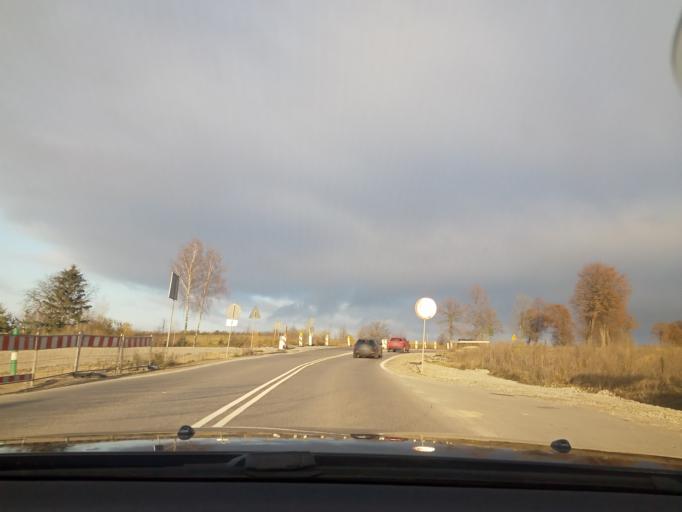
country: PL
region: Lesser Poland Voivodeship
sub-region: Powiat miechowski
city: Miechow
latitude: 50.3190
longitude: 20.0374
